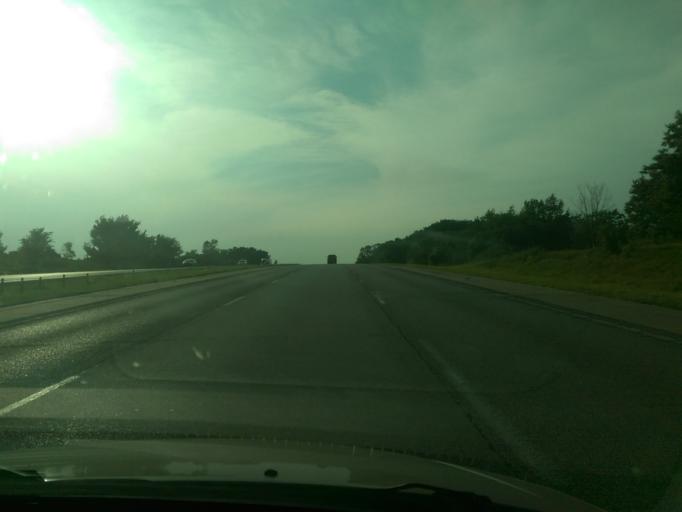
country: US
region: Missouri
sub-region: Platte County
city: Weatherby Lake
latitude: 39.3257
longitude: -94.7052
